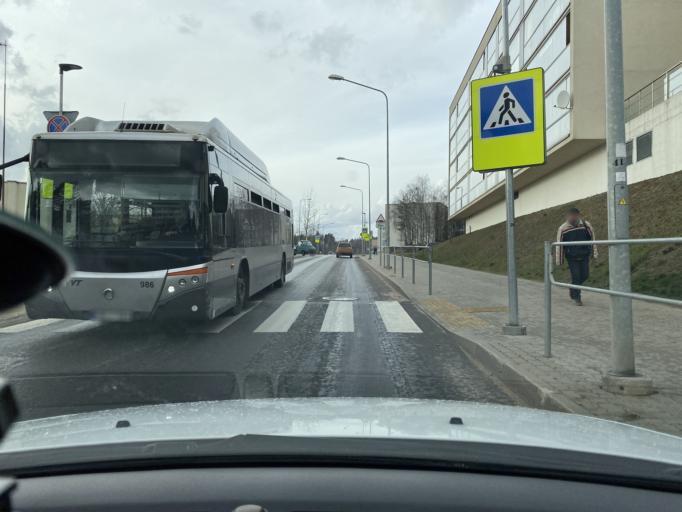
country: LT
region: Vilnius County
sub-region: Vilnius
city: Fabijoniskes
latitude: 54.7542
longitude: 25.2634
